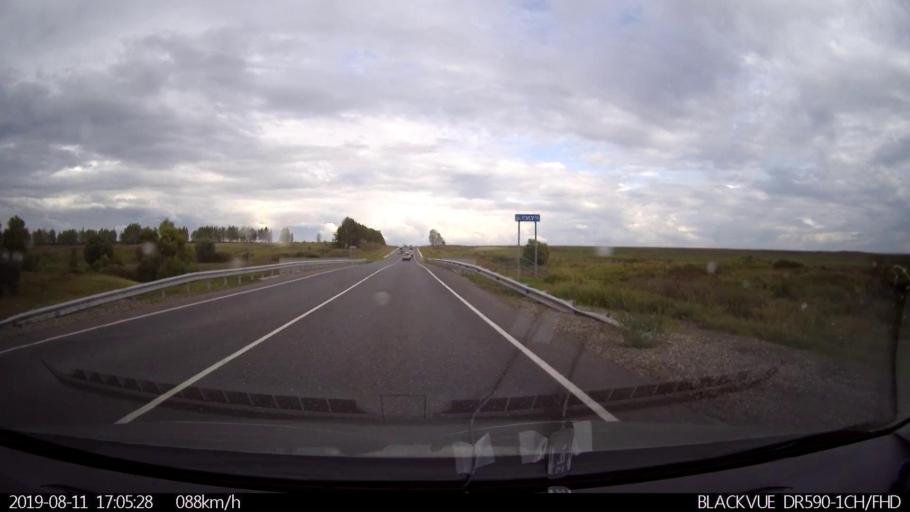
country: RU
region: Ulyanovsk
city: Mayna
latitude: 54.2984
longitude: 47.7864
